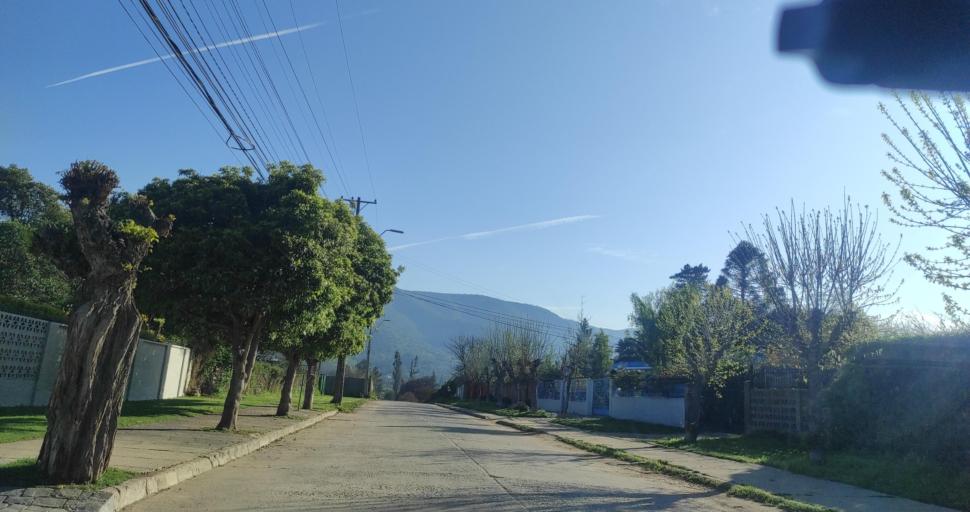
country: CL
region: Valparaiso
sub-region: Provincia de Marga Marga
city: Limache
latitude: -33.0030
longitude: -71.2539
